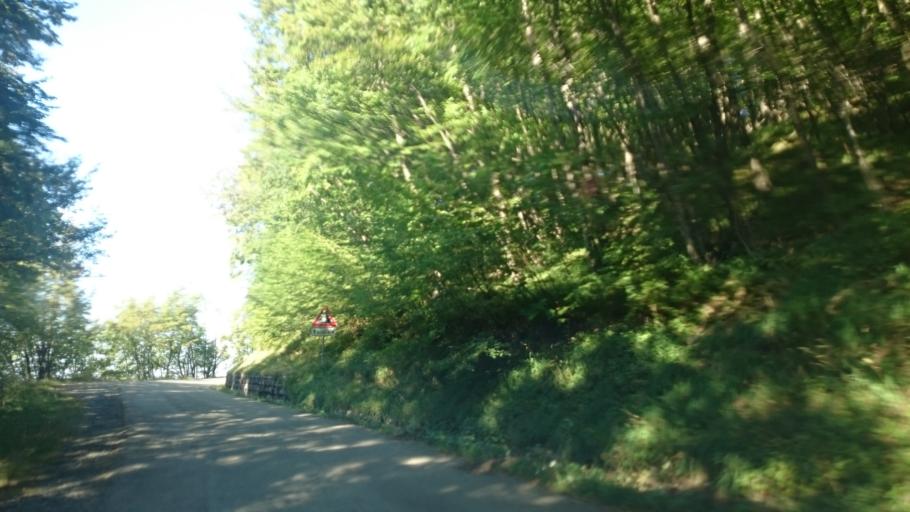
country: IT
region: Emilia-Romagna
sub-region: Provincia di Reggio Emilia
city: Villa Minozzo
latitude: 44.3262
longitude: 10.4688
